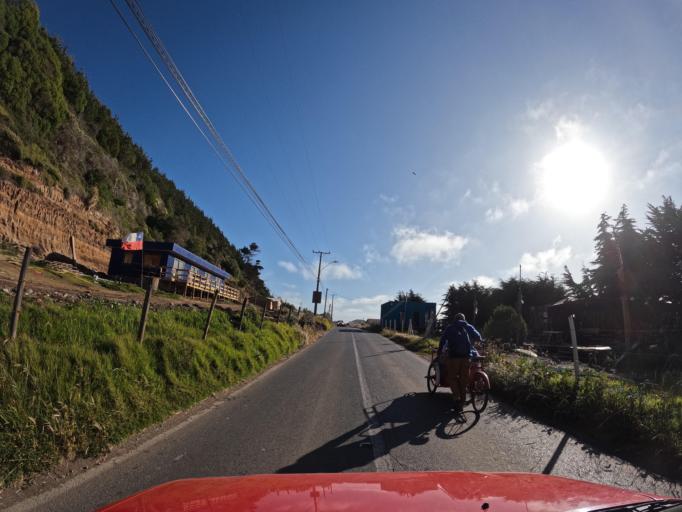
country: CL
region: Maule
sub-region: Provincia de Talca
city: Constitucion
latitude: -34.8916
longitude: -72.1753
